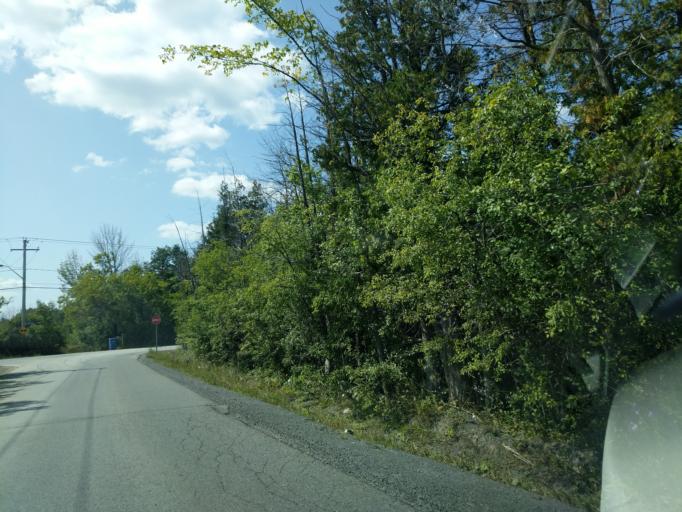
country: CA
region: Ontario
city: Bells Corners
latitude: 45.4358
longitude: -75.9005
